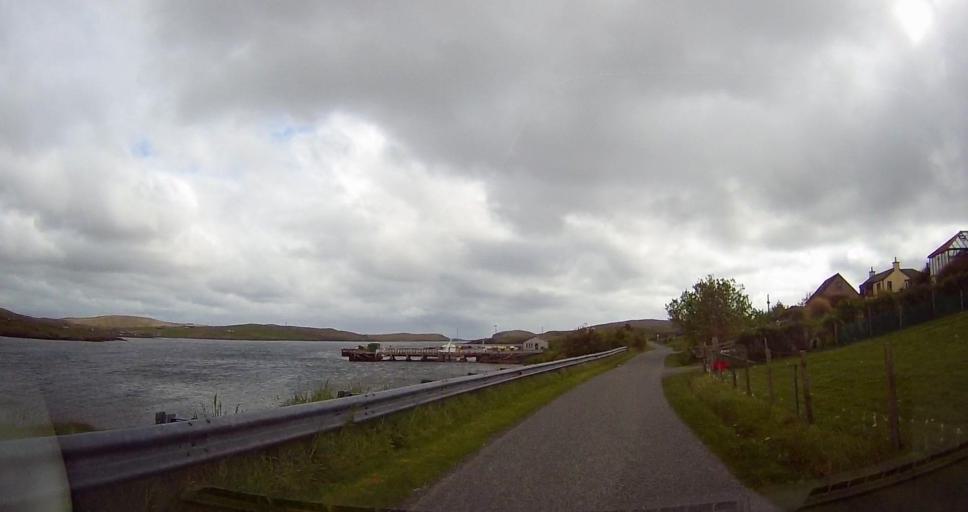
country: GB
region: Scotland
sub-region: Shetland Islands
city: Sandwick
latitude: 60.2259
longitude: -1.5696
